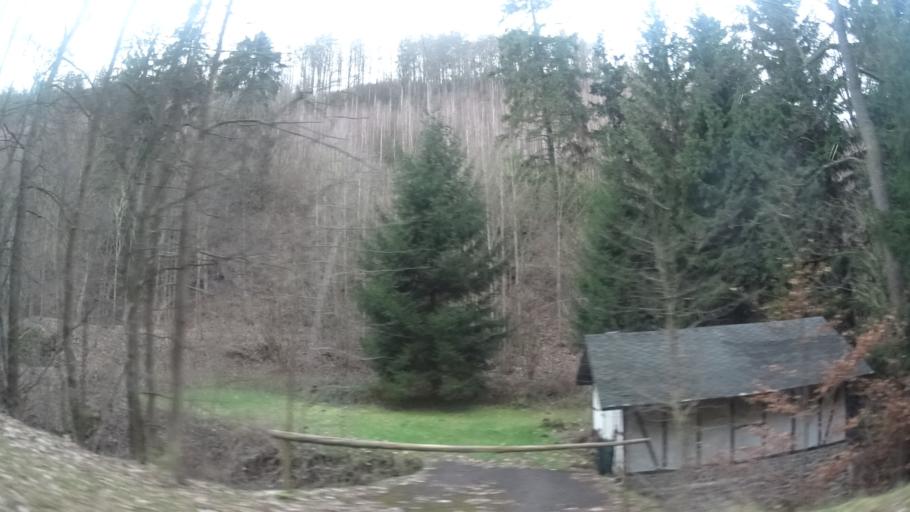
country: DE
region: Thuringia
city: Rohrbach
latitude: 50.6180
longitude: 11.2115
